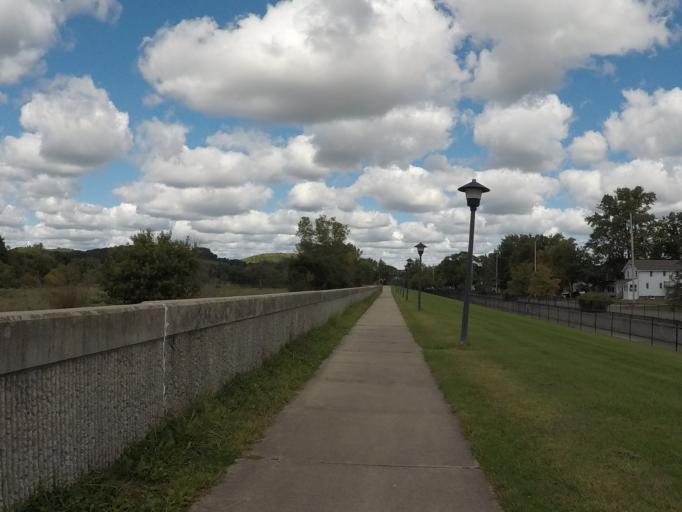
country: US
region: Wisconsin
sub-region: Richland County
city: Richland Center
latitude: 43.3365
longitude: -90.3907
